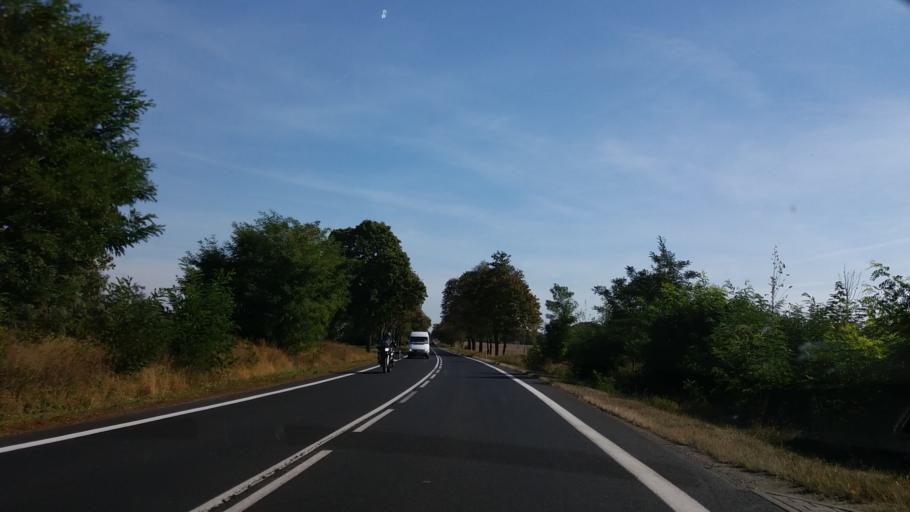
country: PL
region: Greater Poland Voivodeship
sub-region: Powiat miedzychodzki
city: Kwilcz
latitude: 52.5481
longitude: 16.1108
